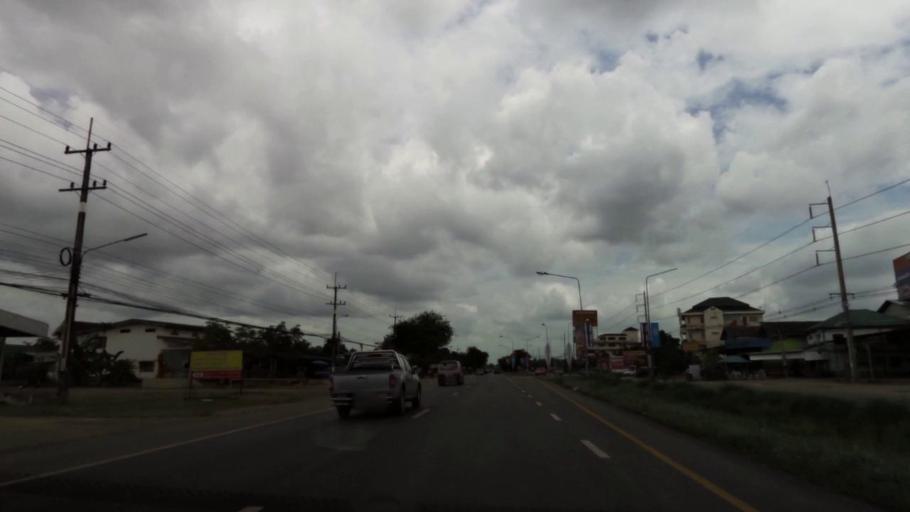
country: TH
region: Rayong
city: Klaeng
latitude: 12.7818
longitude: 101.6937
